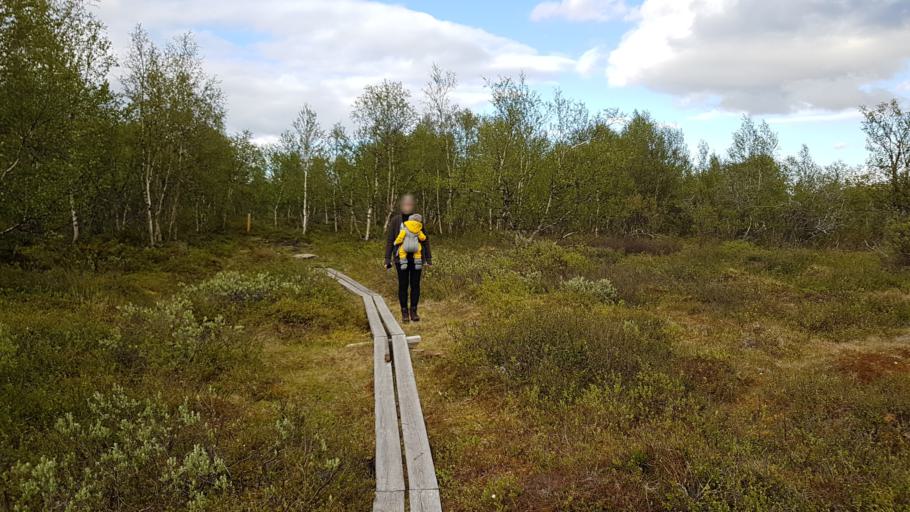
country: NO
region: Troms
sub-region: Bardu
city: Setermoen
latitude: 68.3421
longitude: 18.7728
